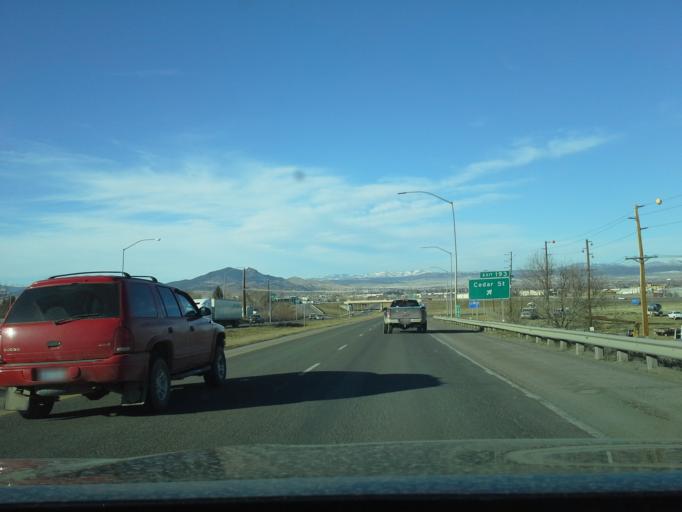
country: US
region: Montana
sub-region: Lewis and Clark County
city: Helena
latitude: 46.6022
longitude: -112.0052
